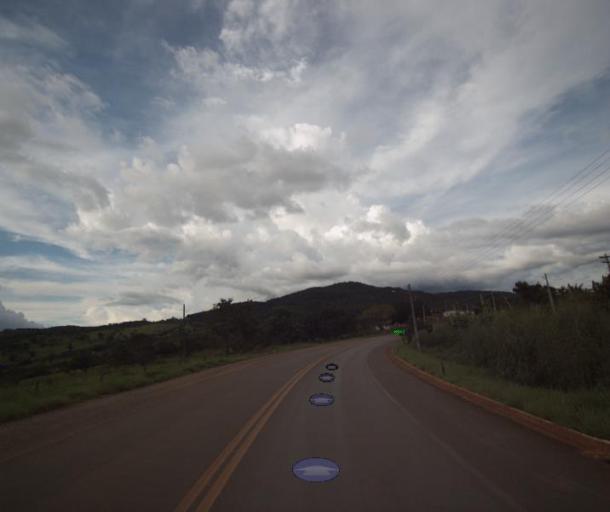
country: BR
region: Goias
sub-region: Niquelandia
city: Niquelandia
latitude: -14.4714
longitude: -48.4882
